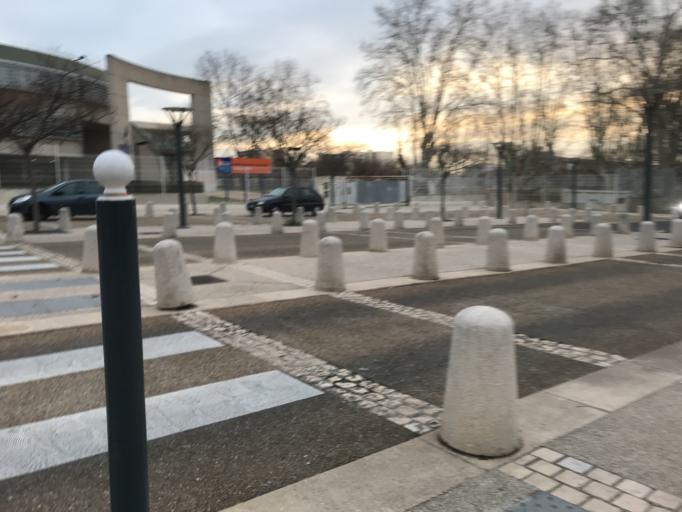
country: FR
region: Languedoc-Roussillon
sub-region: Departement de l'Herault
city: Montpellier
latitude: 43.6102
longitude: 3.8876
